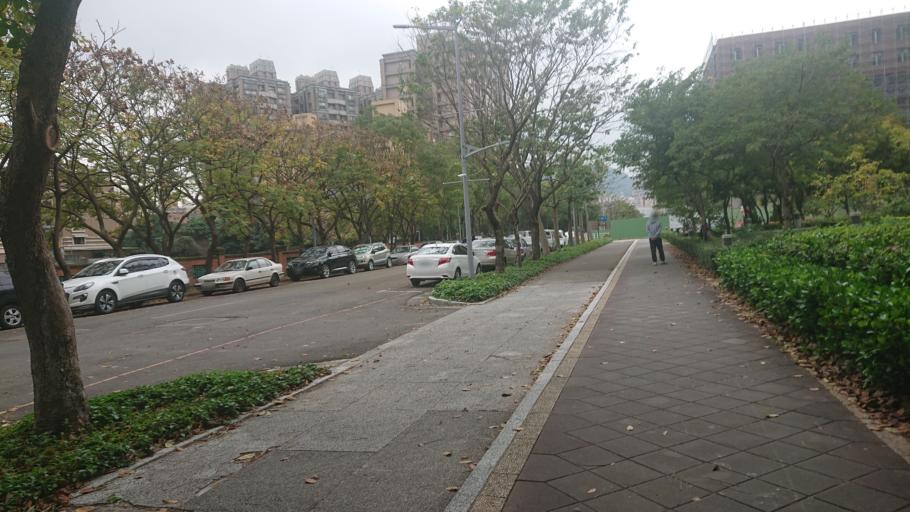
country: TW
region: Taiwan
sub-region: Taoyuan
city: Taoyuan
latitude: 24.9433
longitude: 121.3720
